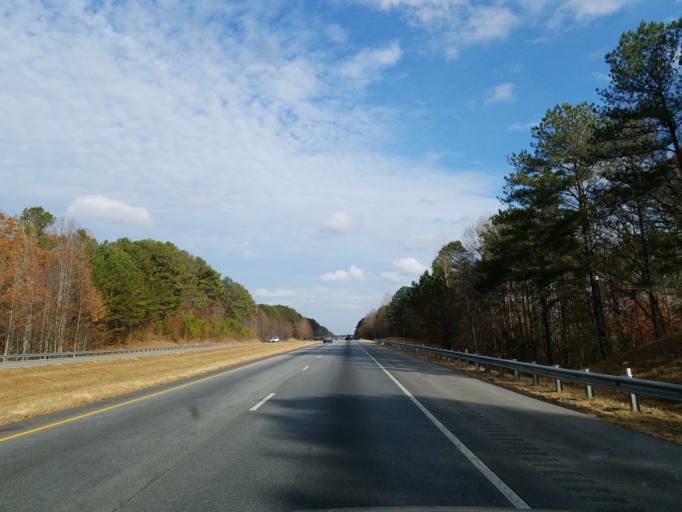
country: US
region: Alabama
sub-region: Cleburne County
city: Heflin
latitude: 33.6266
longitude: -85.5632
